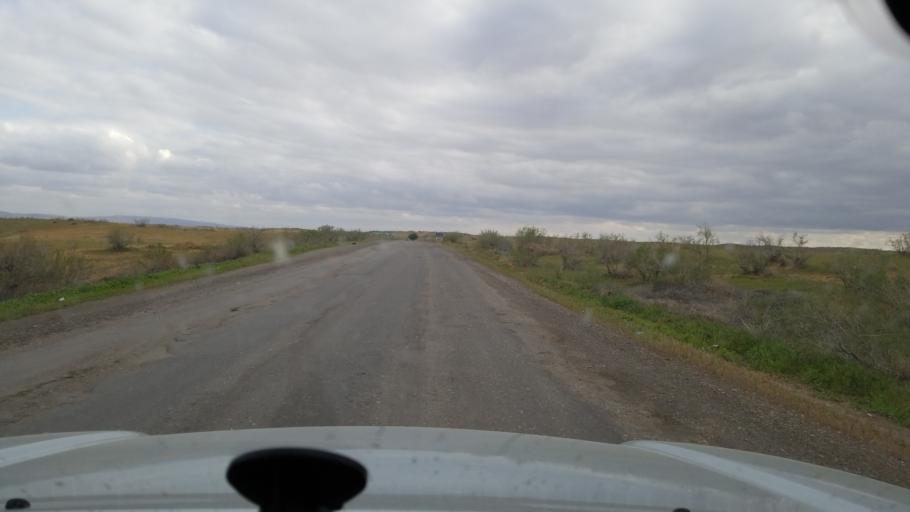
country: TM
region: Mary
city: Serhetabat
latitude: 35.9940
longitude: 62.6272
